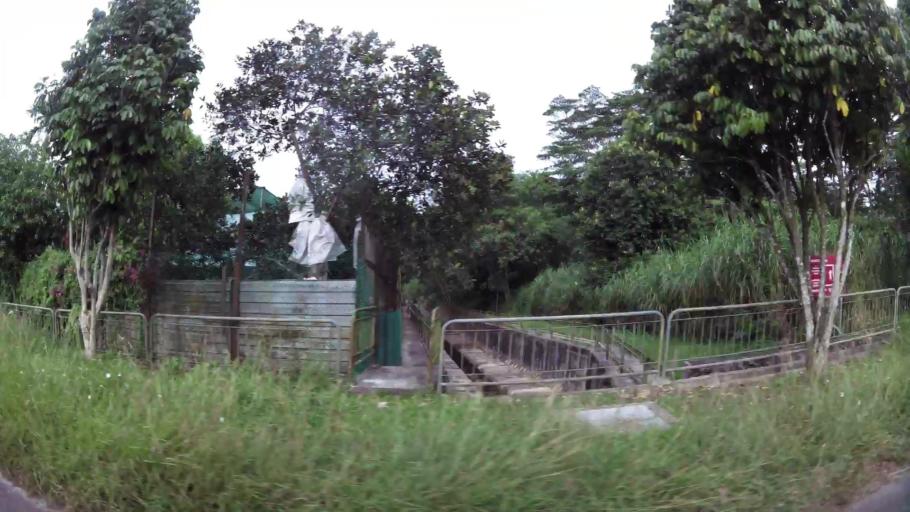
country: MY
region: Johor
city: Johor Bahru
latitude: 1.4417
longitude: 103.7138
